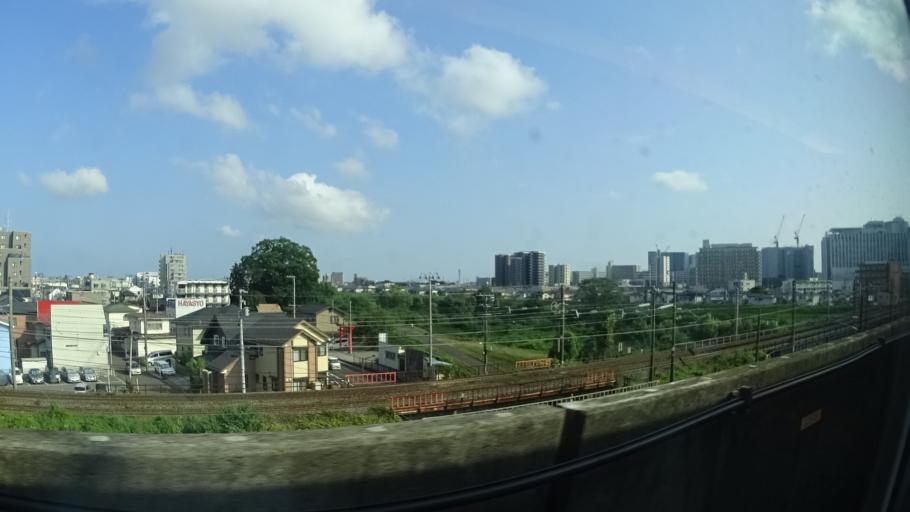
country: JP
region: Miyagi
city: Sendai
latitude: 38.2357
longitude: 140.8917
